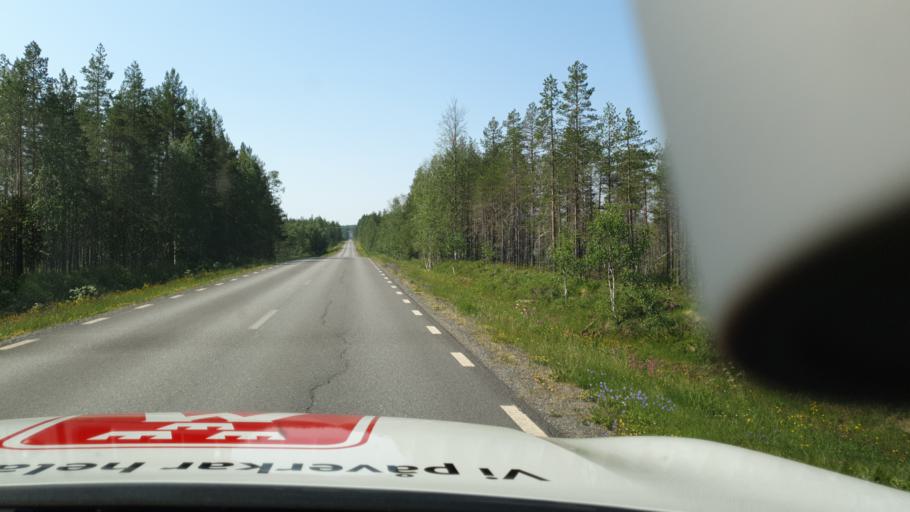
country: SE
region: Vaesterbotten
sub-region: Skelleftea Kommun
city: Langsele
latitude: 64.9888
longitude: 20.0832
